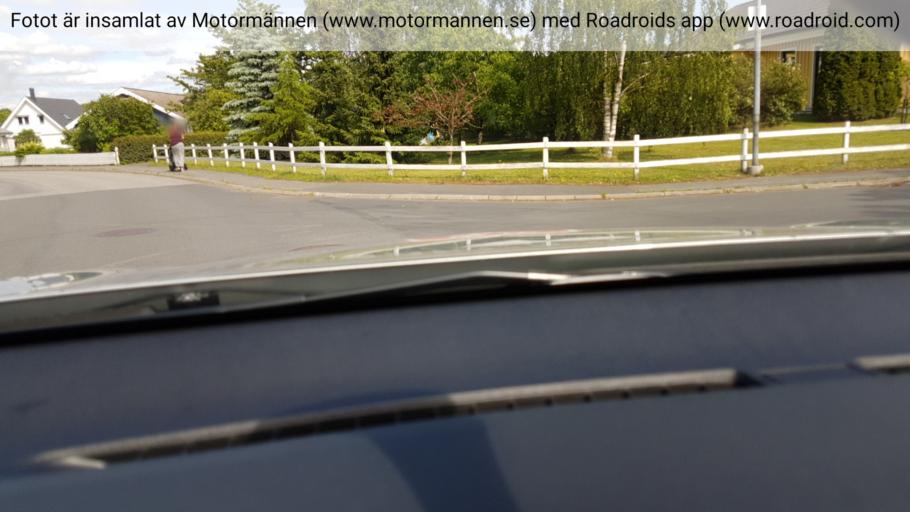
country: SE
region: Joenkoeping
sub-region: Jonkopings Kommun
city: Odensjo
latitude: 57.7498
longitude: 14.1746
